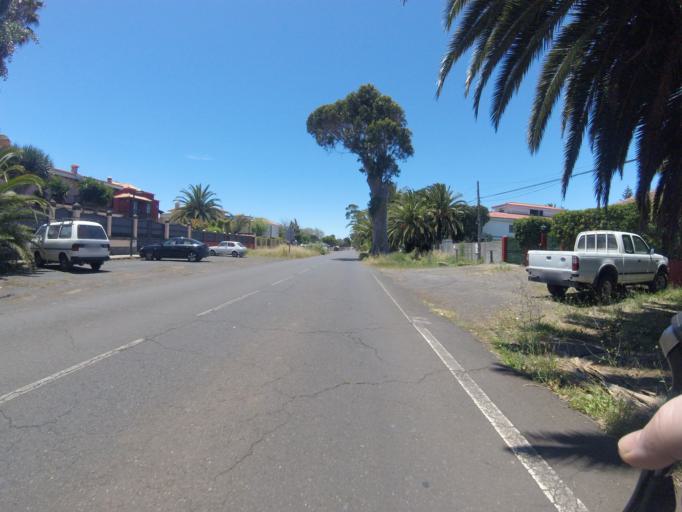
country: ES
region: Canary Islands
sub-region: Provincia de Santa Cruz de Tenerife
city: La Laguna
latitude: 28.4985
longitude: -16.3139
